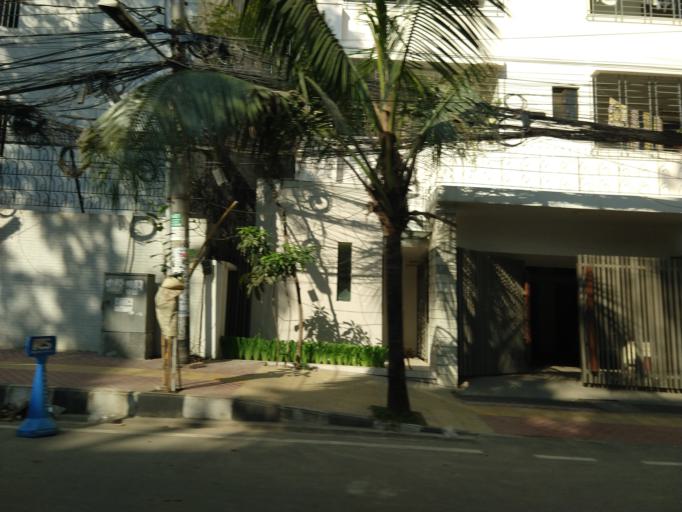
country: BD
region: Dhaka
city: Paltan
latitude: 23.7978
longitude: 90.4119
